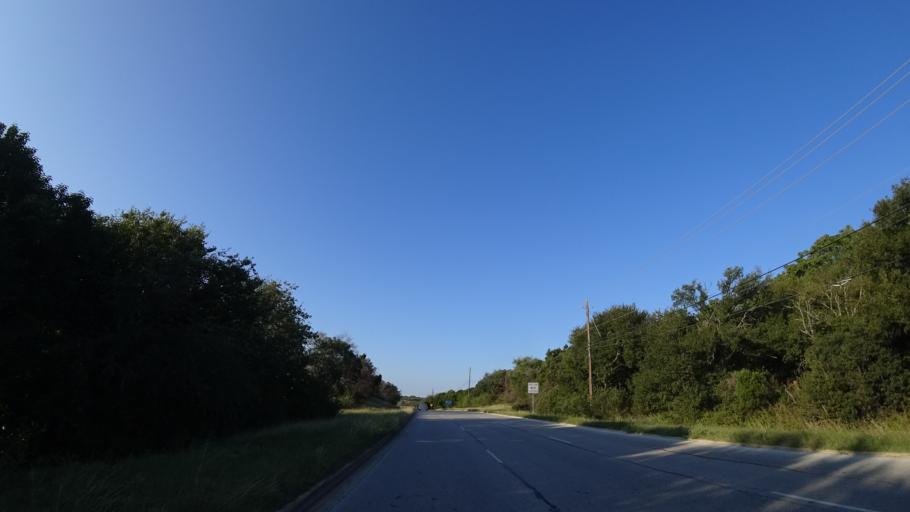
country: US
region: Texas
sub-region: Travis County
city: Rollingwood
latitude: 30.2546
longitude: -97.8046
